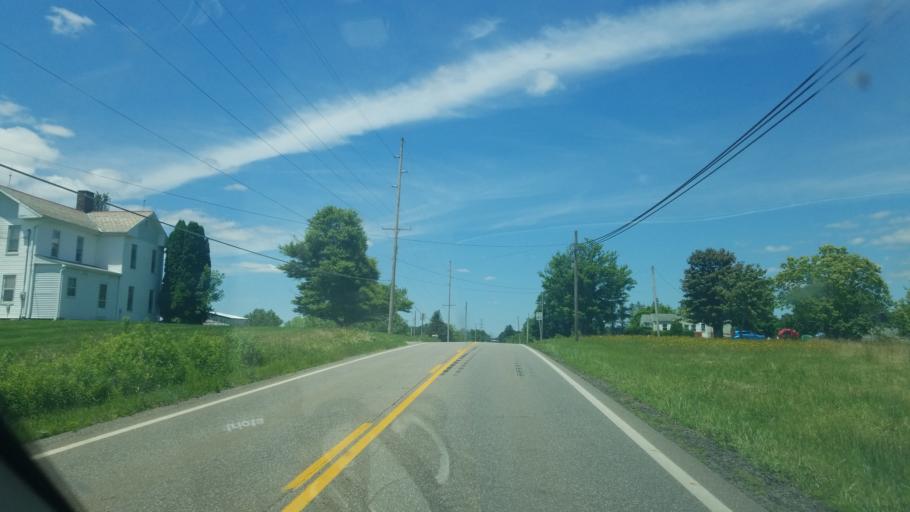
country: US
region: Ohio
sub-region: Columbiana County
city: Lisbon
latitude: 40.8016
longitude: -80.7854
